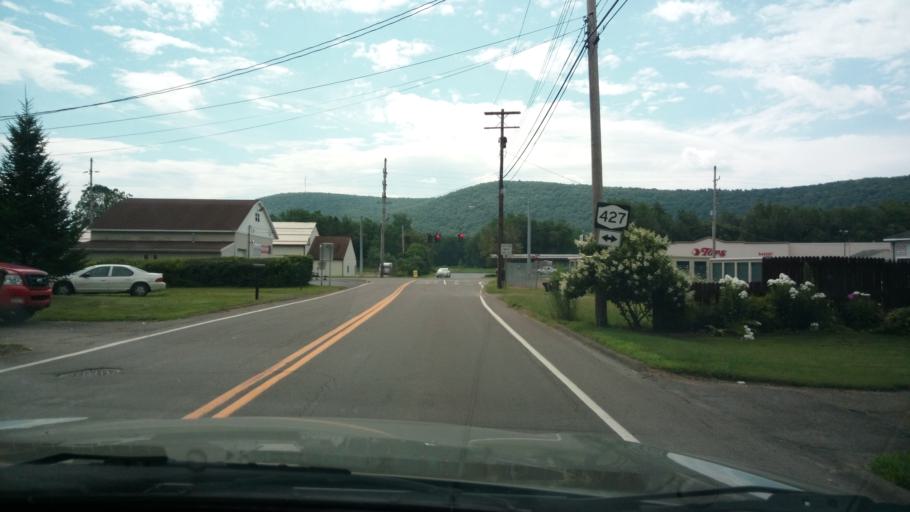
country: US
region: New York
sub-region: Chemung County
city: Southport
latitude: 42.0592
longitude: -76.7930
